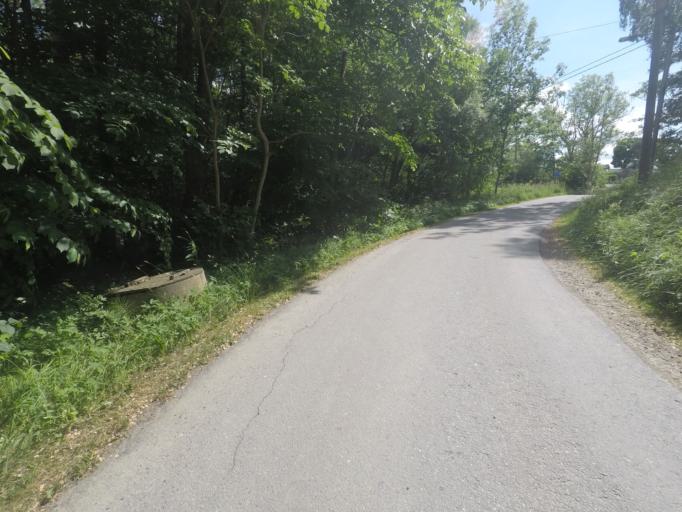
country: SE
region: Vaestra Goetaland
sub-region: Goteborg
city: Billdal
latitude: 57.5771
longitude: 11.9518
